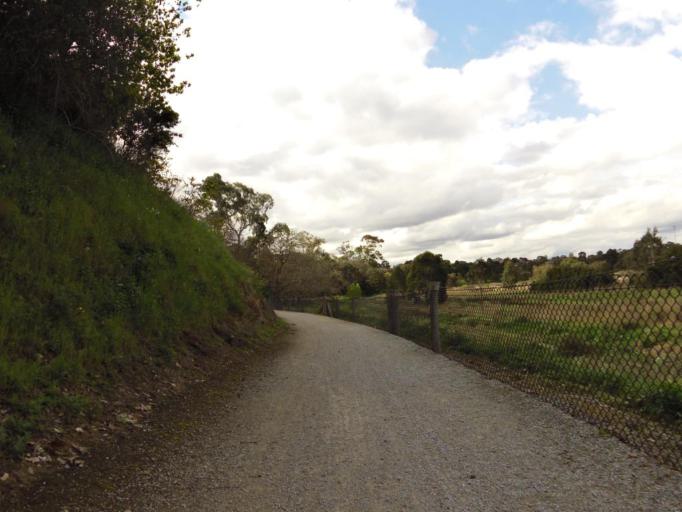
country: AU
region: Victoria
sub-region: Banyule
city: Viewbank
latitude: -37.7484
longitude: 145.0844
